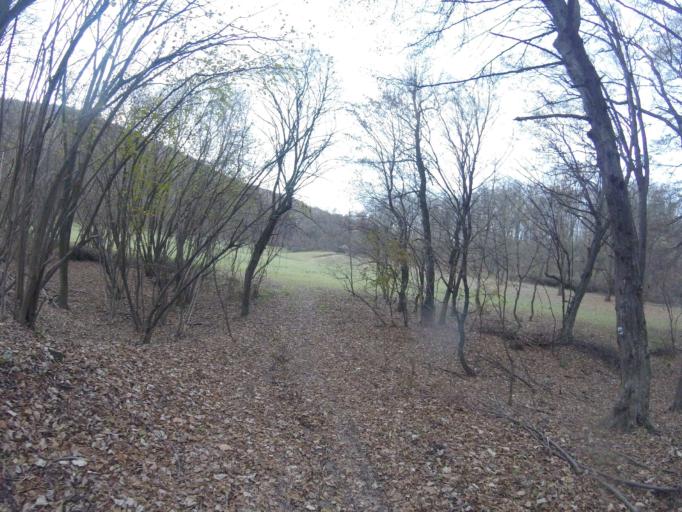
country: HU
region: Tolna
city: Szentgalpuszta
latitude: 46.3288
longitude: 18.6286
